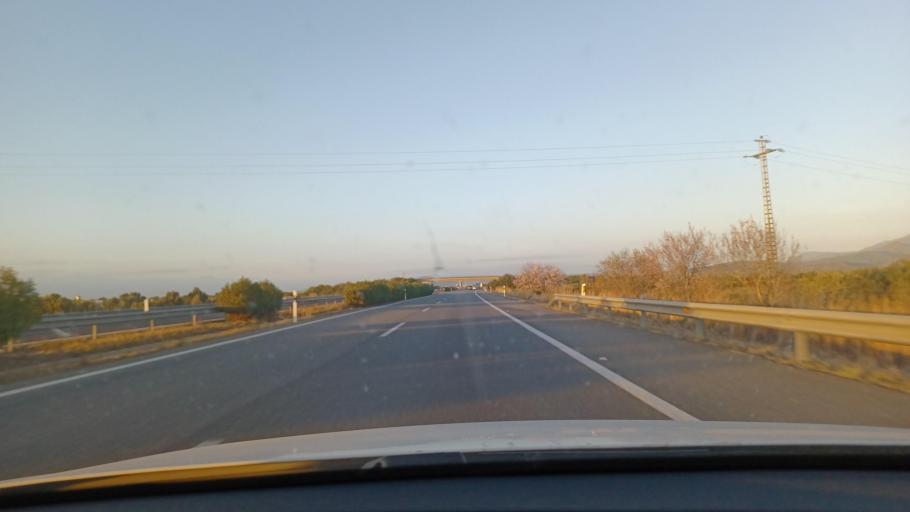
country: ES
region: Catalonia
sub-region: Provincia de Tarragona
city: Alcanar
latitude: 40.5217
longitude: 0.4165
